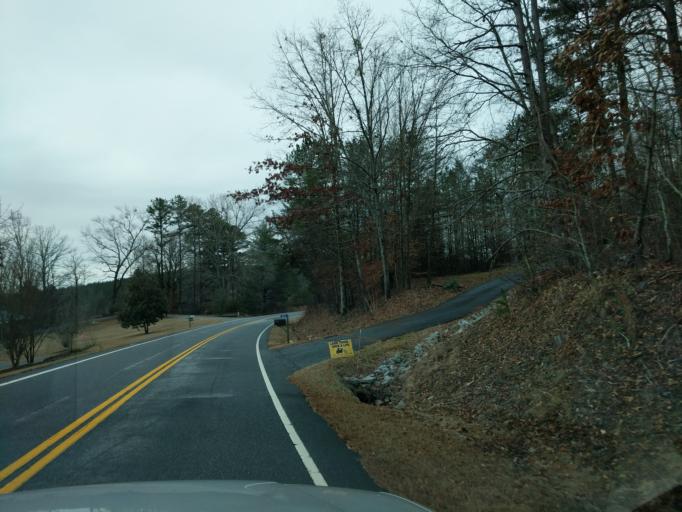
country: US
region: South Carolina
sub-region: Oconee County
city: Walhalla
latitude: 34.8166
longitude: -83.0464
